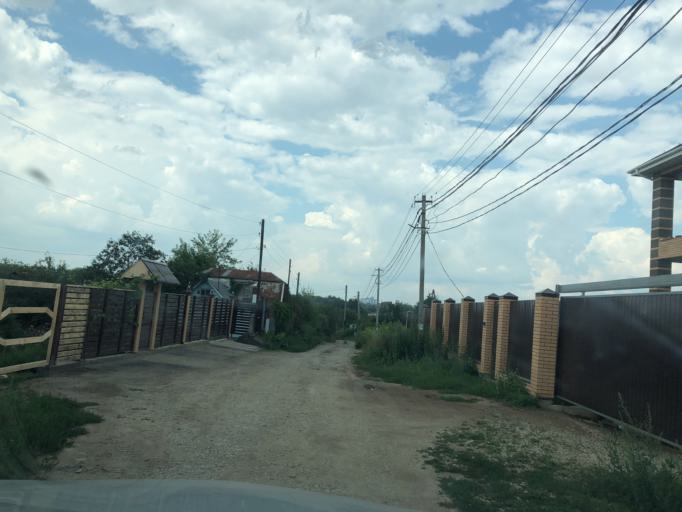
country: RU
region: Tula
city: Mendeleyevskiy
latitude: 54.1591
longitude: 37.5639
